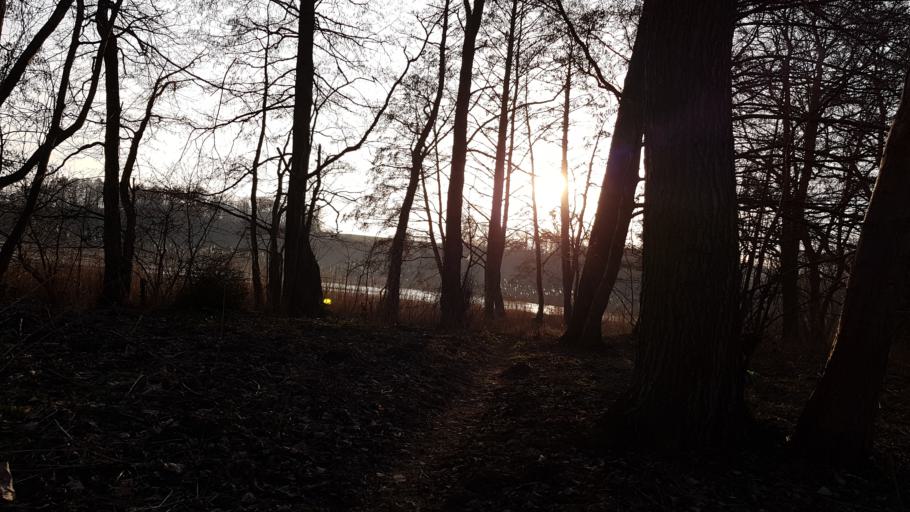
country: PL
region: West Pomeranian Voivodeship
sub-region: Powiat mysliborski
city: Barlinek
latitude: 52.9833
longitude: 15.2018
